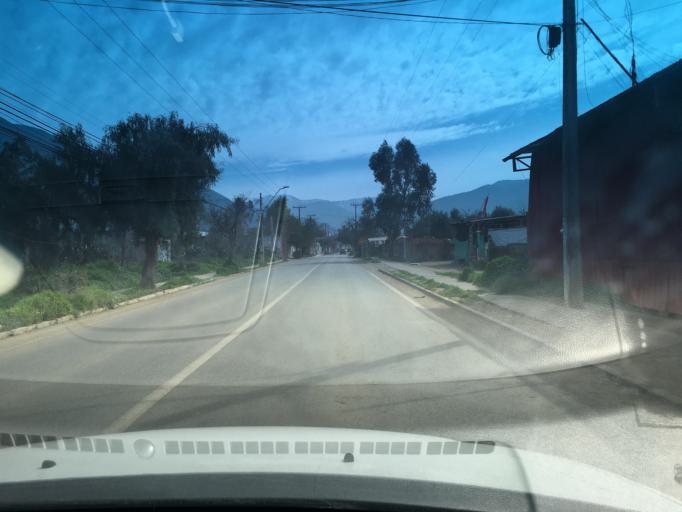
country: CL
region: Santiago Metropolitan
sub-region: Provincia de Chacabuco
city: Lampa
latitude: -33.0880
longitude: -70.9289
